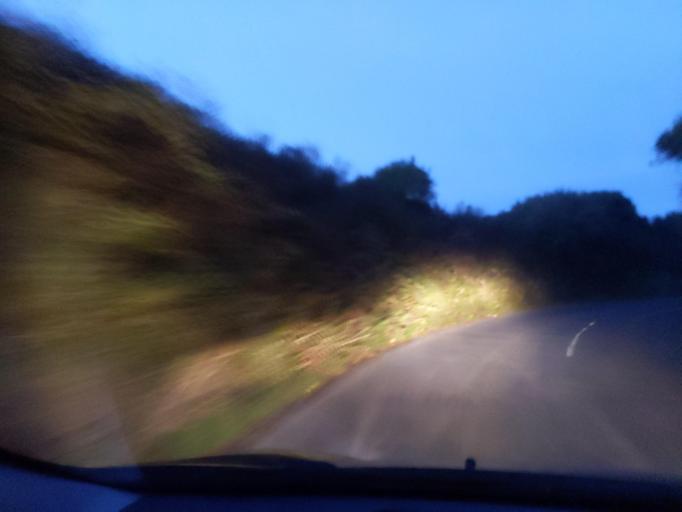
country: GB
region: England
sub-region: Cornwall
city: Camelford
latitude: 50.7006
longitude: -4.6505
